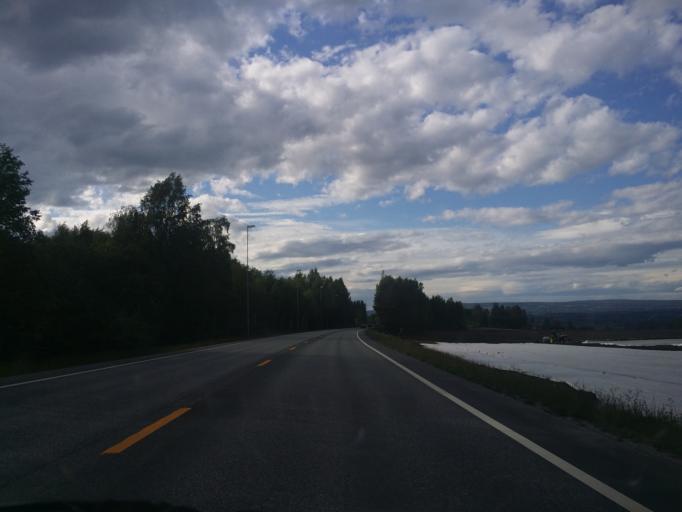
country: NO
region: Hedmark
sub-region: Stange
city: Stange
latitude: 60.7494
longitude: 11.1979
